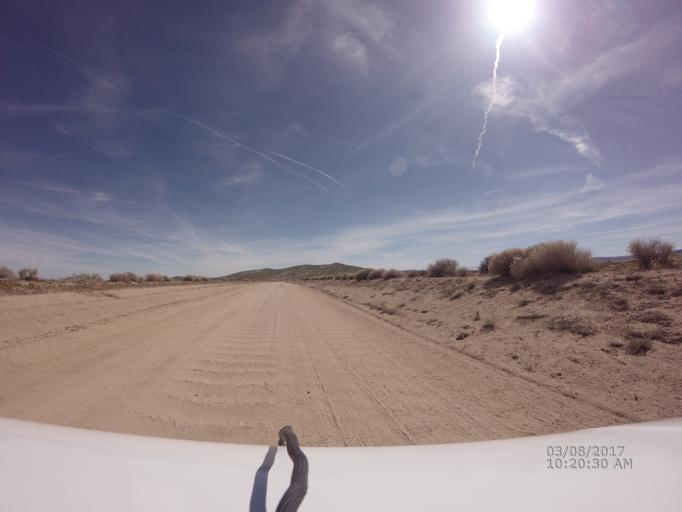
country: US
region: California
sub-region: Los Angeles County
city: Green Valley
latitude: 34.7533
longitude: -118.4340
